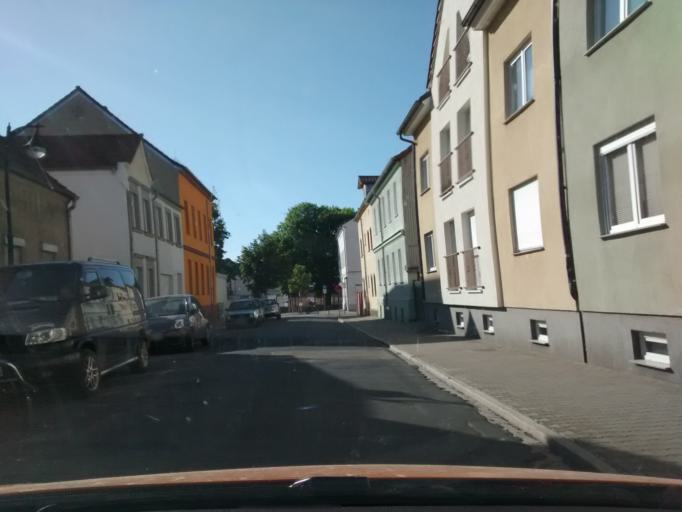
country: DE
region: Brandenburg
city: Furstenwalde
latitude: 52.3623
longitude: 14.0644
